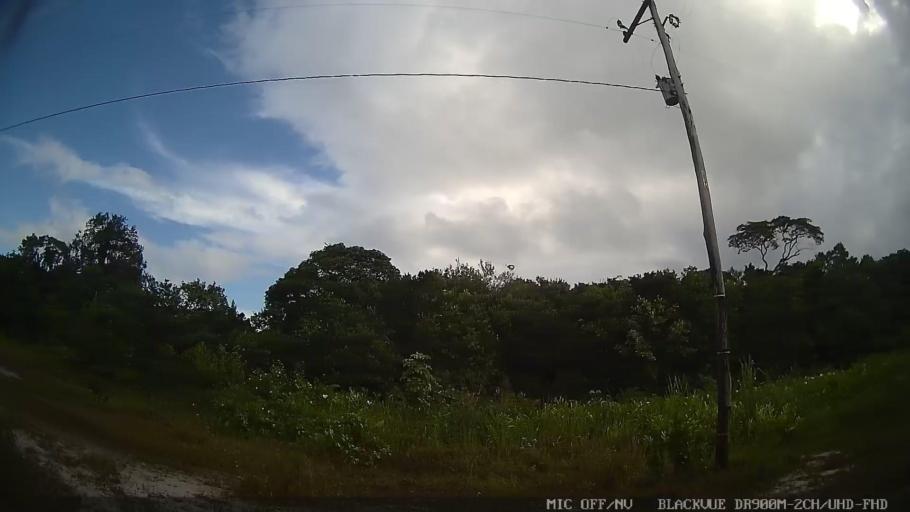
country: BR
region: Sao Paulo
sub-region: Itanhaem
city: Itanhaem
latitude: -24.1749
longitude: -46.9272
